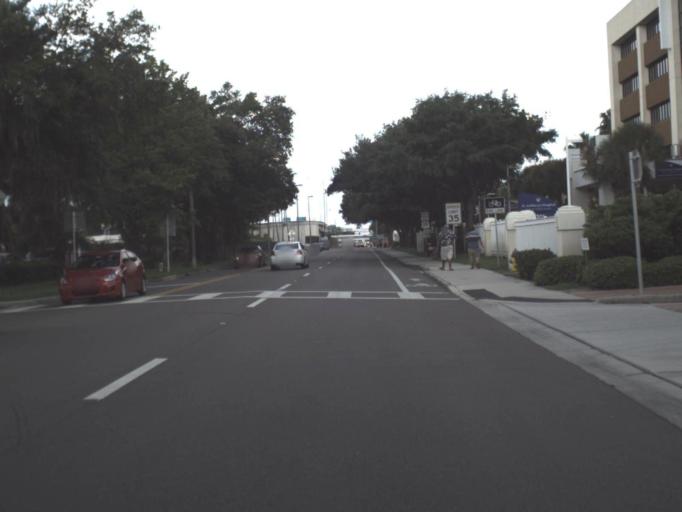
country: US
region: Florida
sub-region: Pinellas County
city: Saint Petersburg
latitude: 27.7776
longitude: -82.6503
